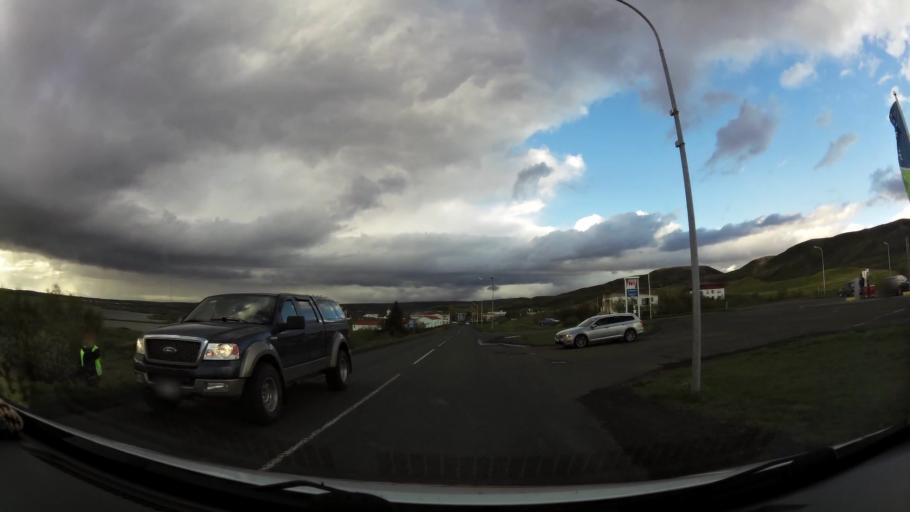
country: IS
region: Northeast
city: Laugar
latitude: 65.6415
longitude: -16.9117
